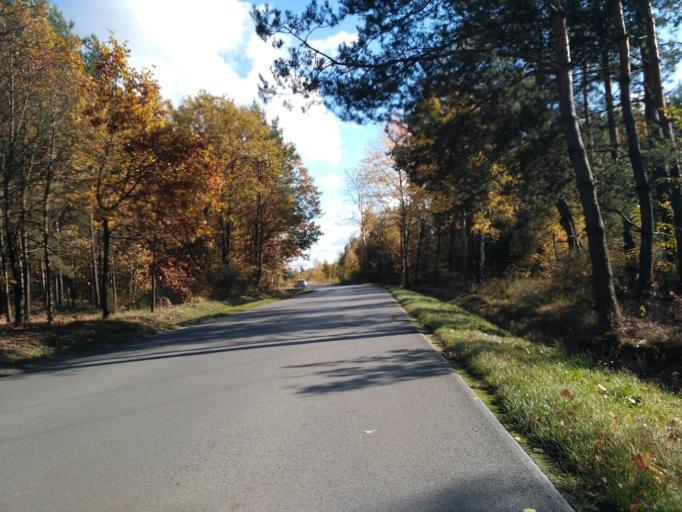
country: PL
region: Subcarpathian Voivodeship
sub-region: Powiat rzeszowski
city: Glogow Malopolski
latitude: 50.1555
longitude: 21.9252
